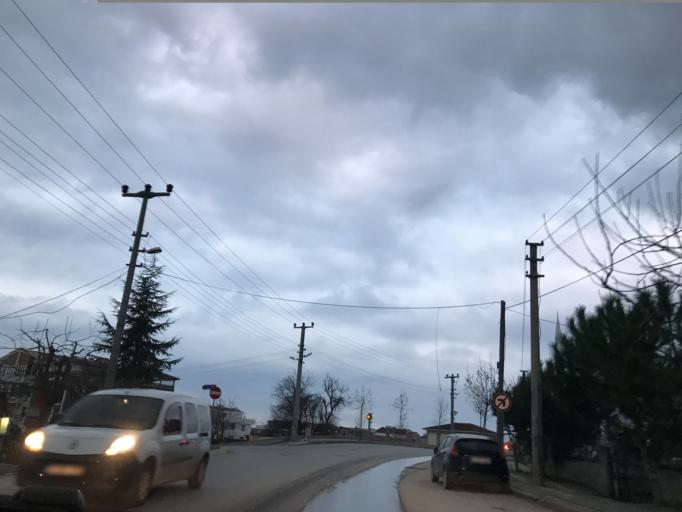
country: TR
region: Yalova
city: Yalova
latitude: 40.6390
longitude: 29.2615
